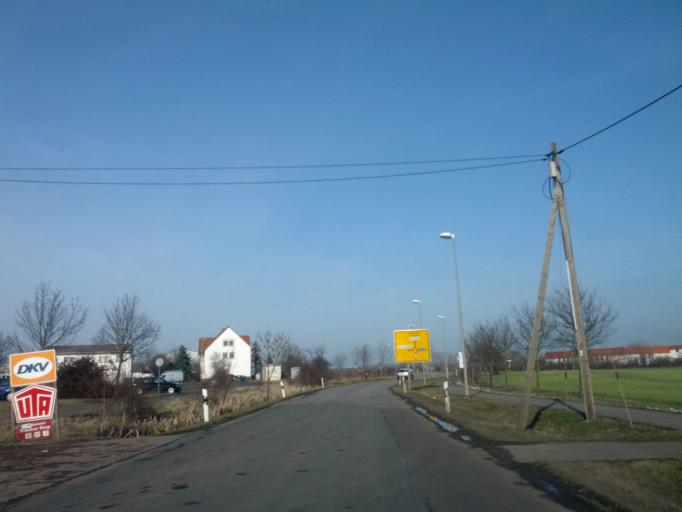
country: DE
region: Thuringia
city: Wandersleben
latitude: 50.8905
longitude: 10.8486
